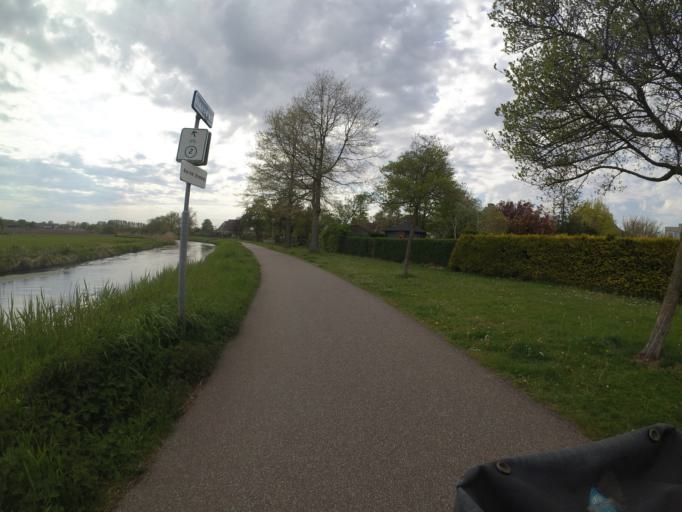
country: NL
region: North Brabant
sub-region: Gemeente Boxtel
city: Boxtel
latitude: 51.5821
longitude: 5.3494
